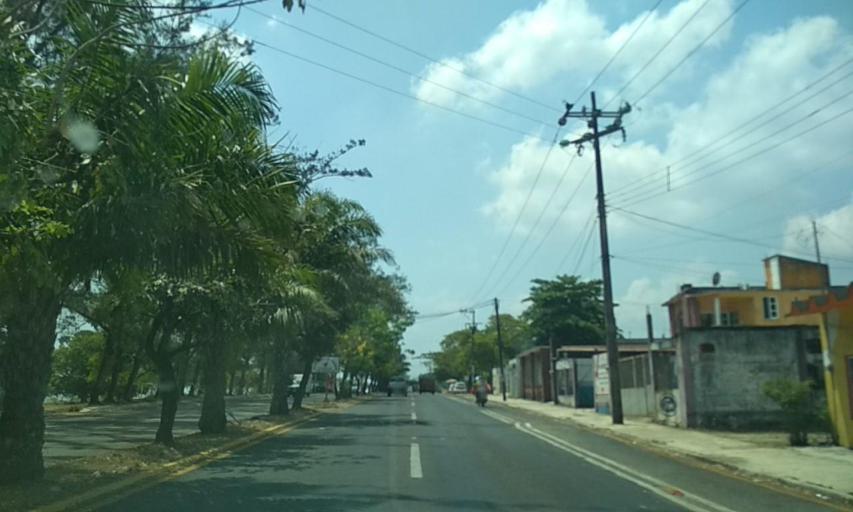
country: MX
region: Veracruz
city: Las Choapas
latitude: 17.9312
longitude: -94.0974
